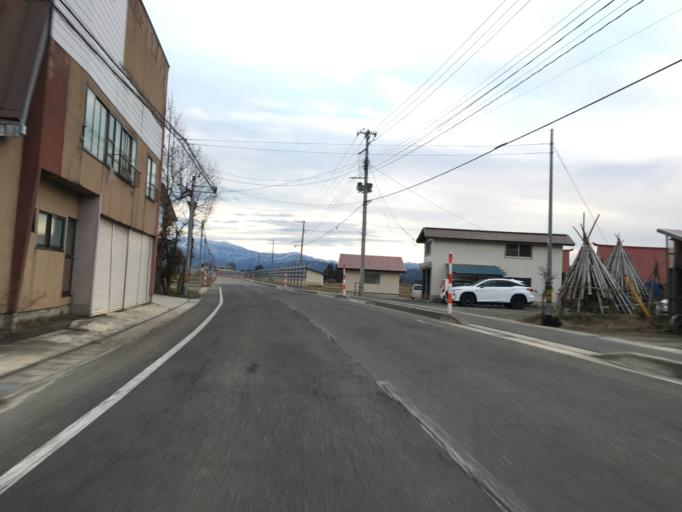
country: JP
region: Yamagata
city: Yonezawa
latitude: 37.9896
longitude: 140.0761
